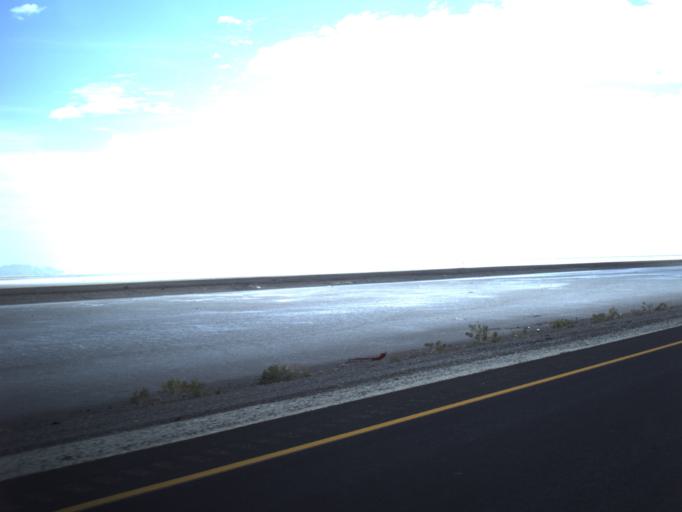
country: US
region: Utah
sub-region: Tooele County
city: Wendover
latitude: 40.7336
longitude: -113.6196
